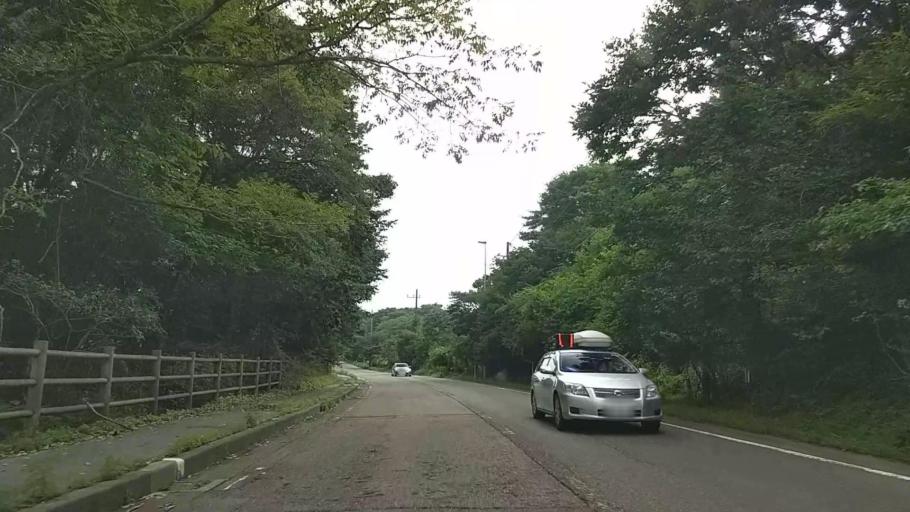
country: JP
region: Yamanashi
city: Fujikawaguchiko
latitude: 35.4357
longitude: 138.5993
